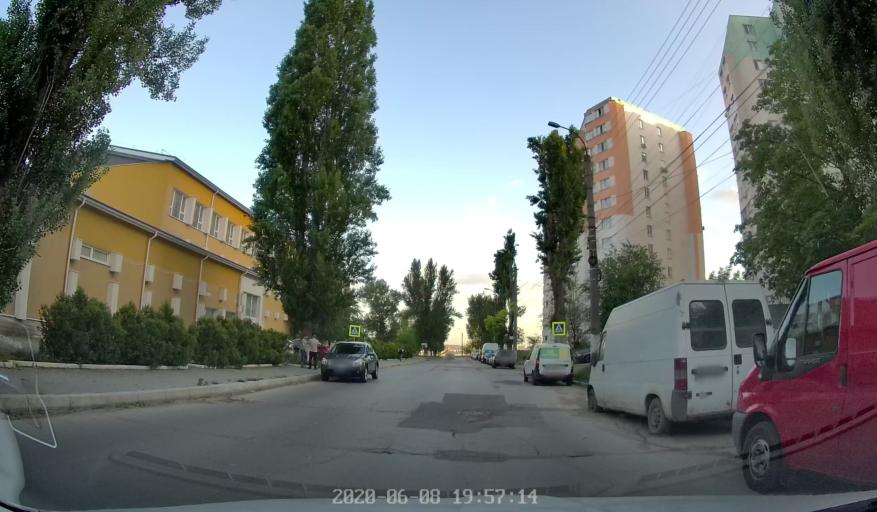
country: MD
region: Chisinau
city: Chisinau
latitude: 47.0170
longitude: 28.8826
